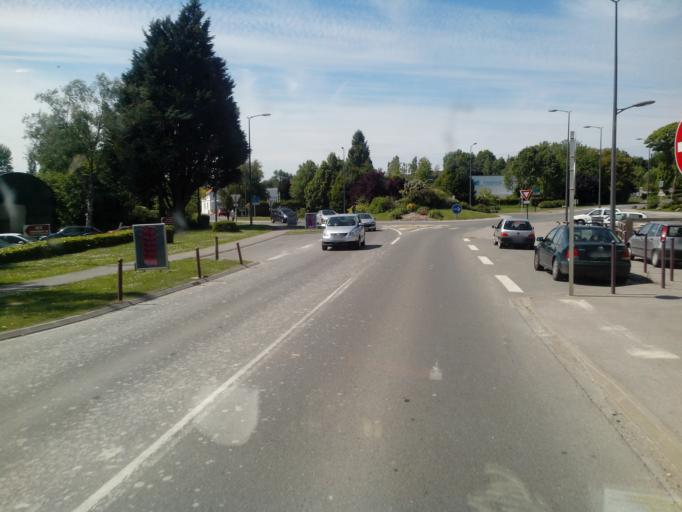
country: FR
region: Nord-Pas-de-Calais
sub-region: Departement du Pas-de-Calais
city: Montreuil
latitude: 50.4809
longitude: 1.7645
